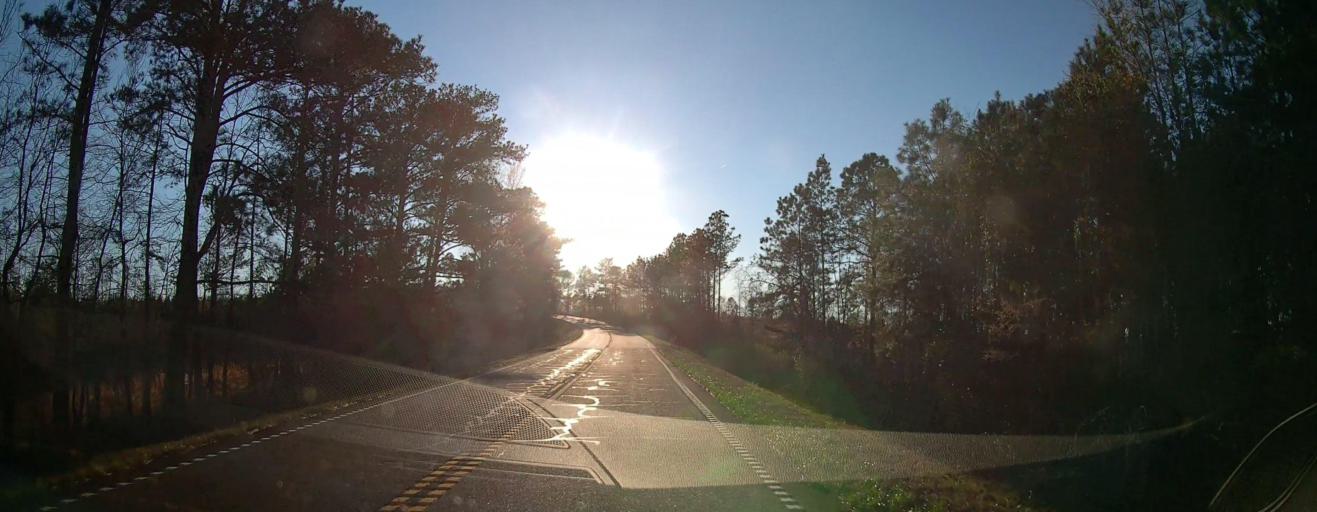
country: US
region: Georgia
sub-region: Talbot County
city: Talbotton
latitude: 32.6475
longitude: -84.6933
